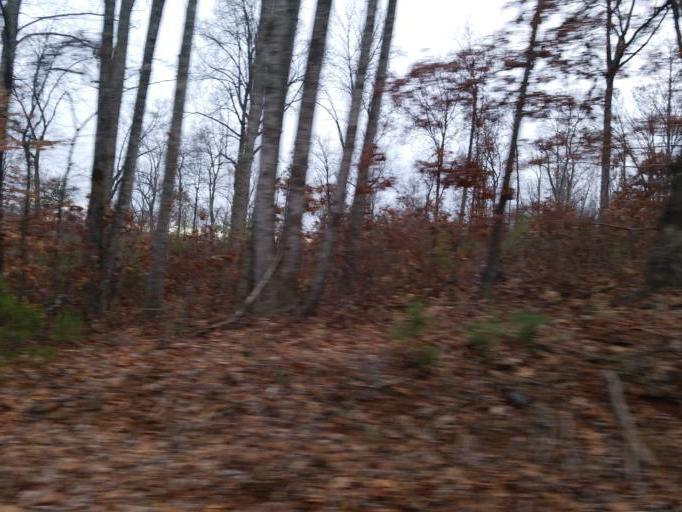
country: US
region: Georgia
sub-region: Dawson County
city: Dawsonville
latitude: 34.4322
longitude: -84.0608
